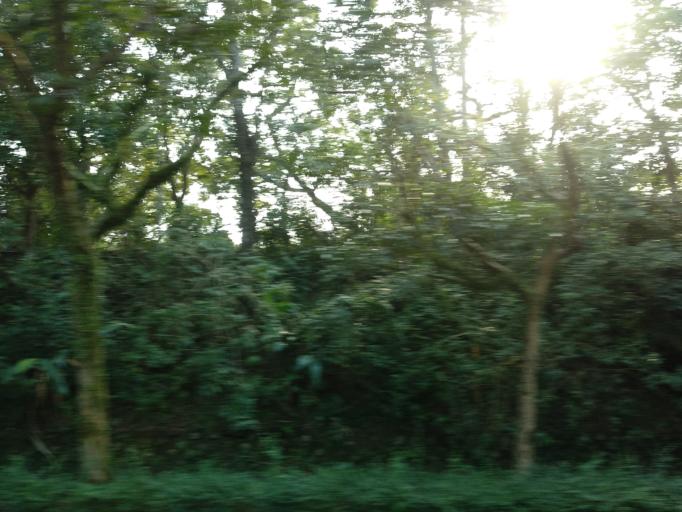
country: TW
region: Taiwan
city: Daxi
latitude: 24.8253
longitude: 121.1808
